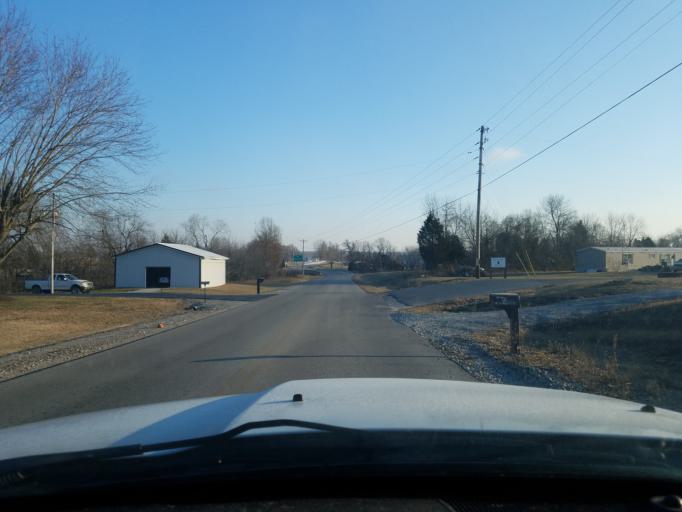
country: US
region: Kentucky
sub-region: Ohio County
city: Beaver Dam
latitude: 37.3701
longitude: -86.8355
